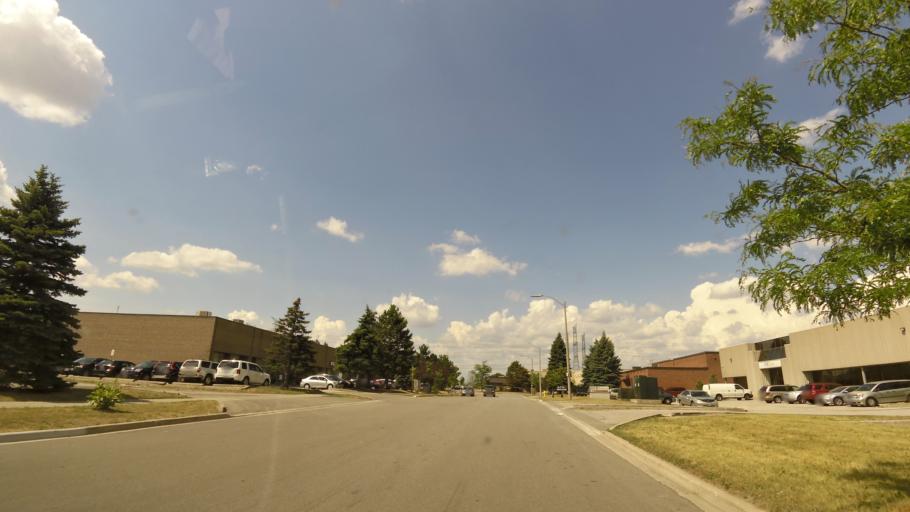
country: CA
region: Ontario
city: Concord
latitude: 43.7758
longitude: -79.5274
